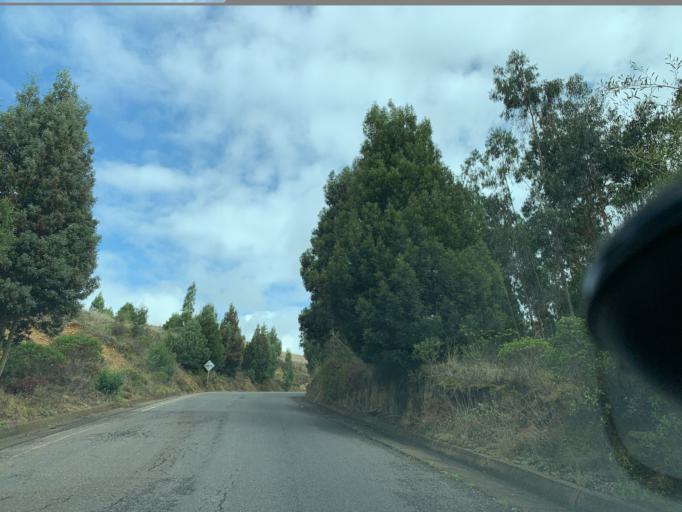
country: CO
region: Boyaca
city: Tunja
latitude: 5.5661
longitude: -73.3624
